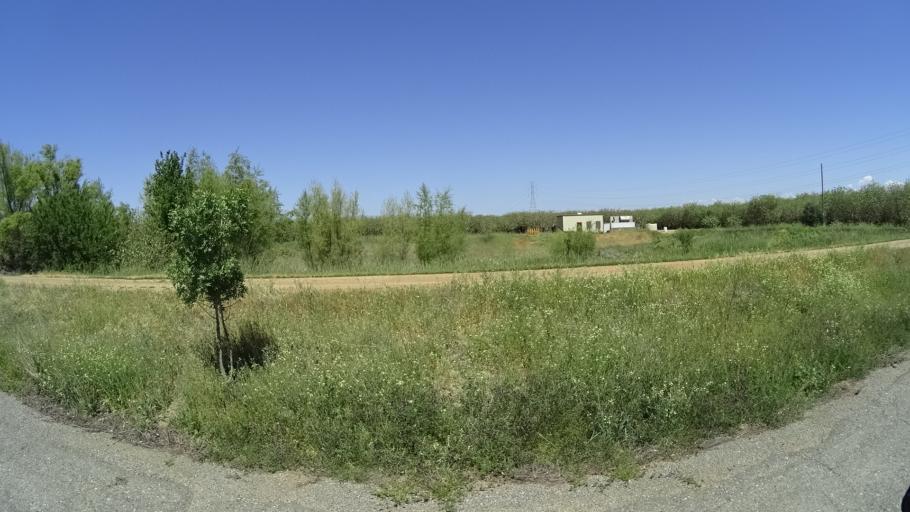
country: US
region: California
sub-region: Glenn County
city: Orland
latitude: 39.7795
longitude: -122.1462
